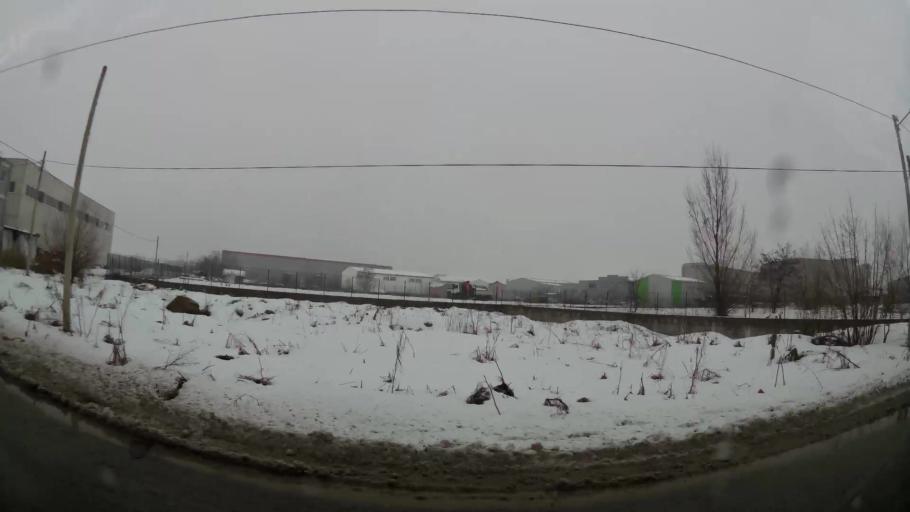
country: RS
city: Novi Banovci
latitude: 44.8841
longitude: 20.3150
